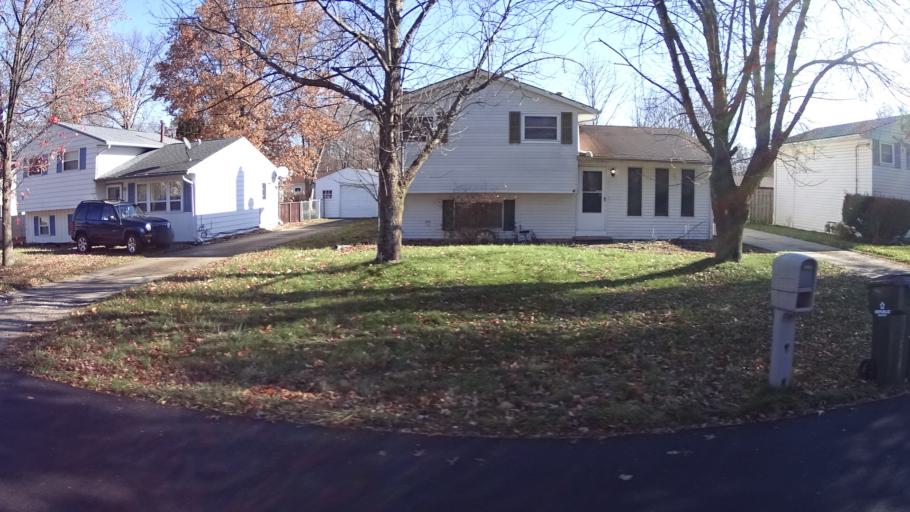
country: US
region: Ohio
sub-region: Lorain County
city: North Ridgeville
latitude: 41.4094
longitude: -81.9996
